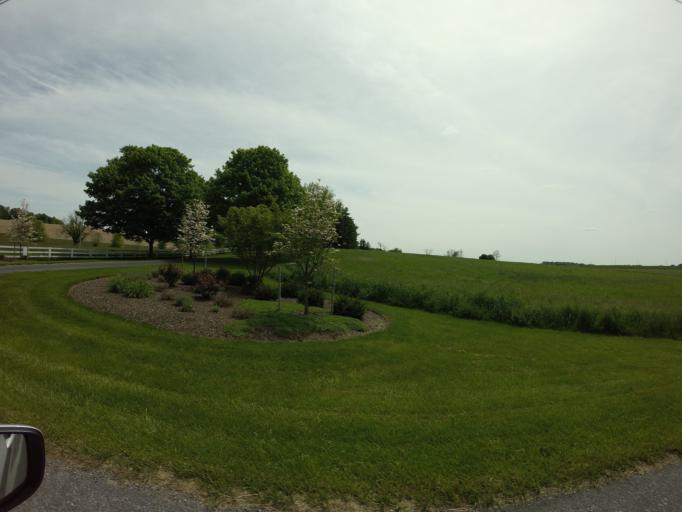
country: US
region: Maryland
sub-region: Frederick County
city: Linganore
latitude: 39.4926
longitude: -77.1725
